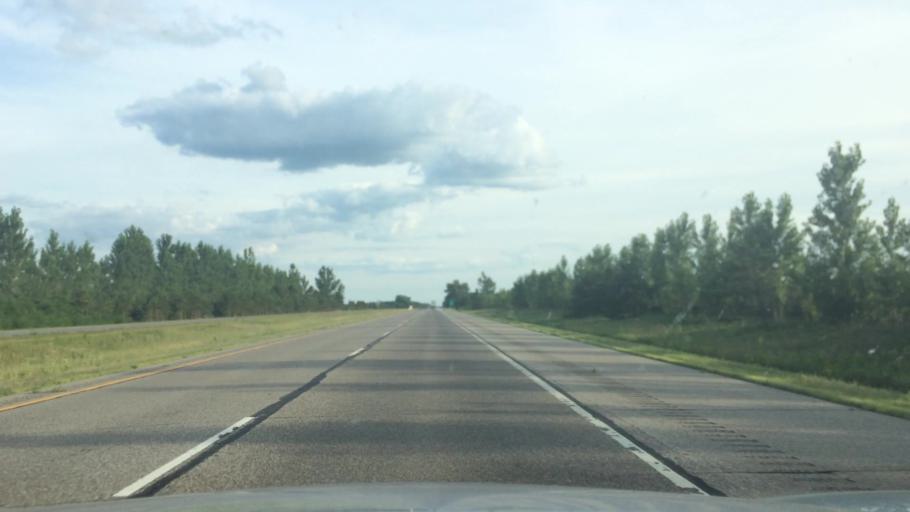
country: US
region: Wisconsin
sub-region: Portage County
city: Plover
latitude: 44.2843
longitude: -89.5237
